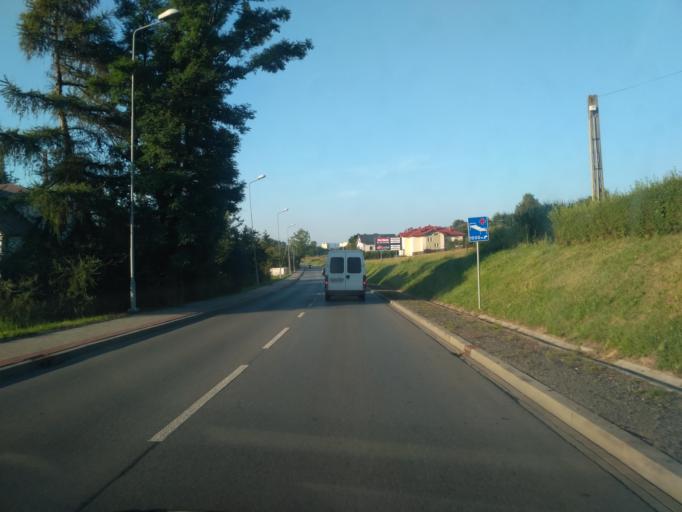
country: PL
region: Subcarpathian Voivodeship
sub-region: Krosno
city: Krosno
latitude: 49.7032
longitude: 21.7867
